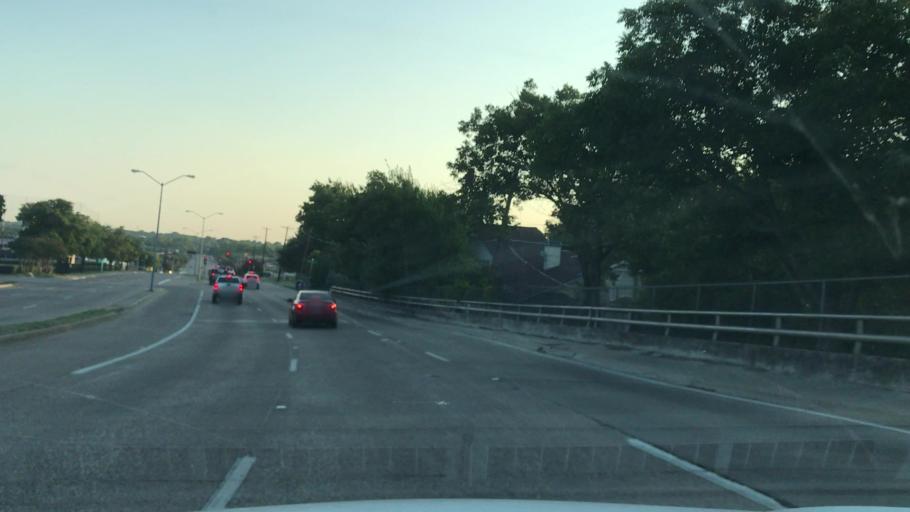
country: US
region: Texas
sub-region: Dallas County
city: Highland Park
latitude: 32.8606
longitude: -96.7451
